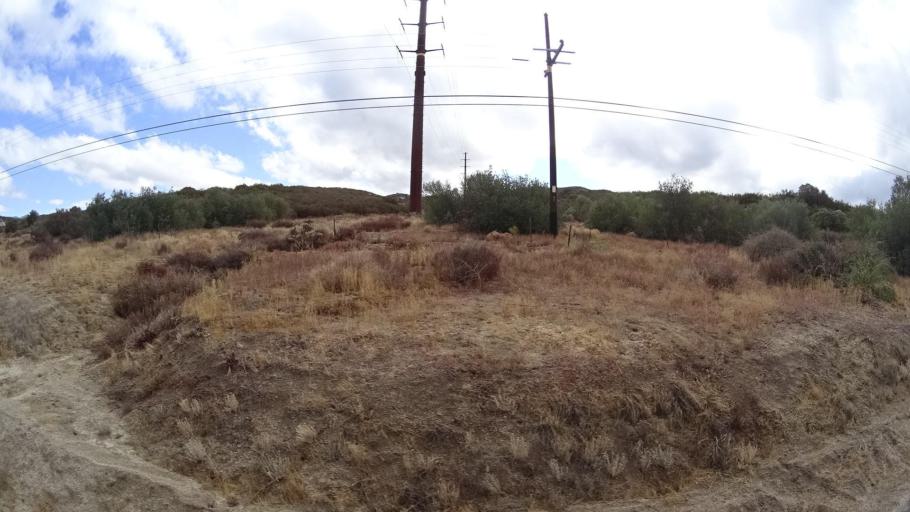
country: US
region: California
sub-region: San Diego County
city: Campo
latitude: 32.7163
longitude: -116.4297
